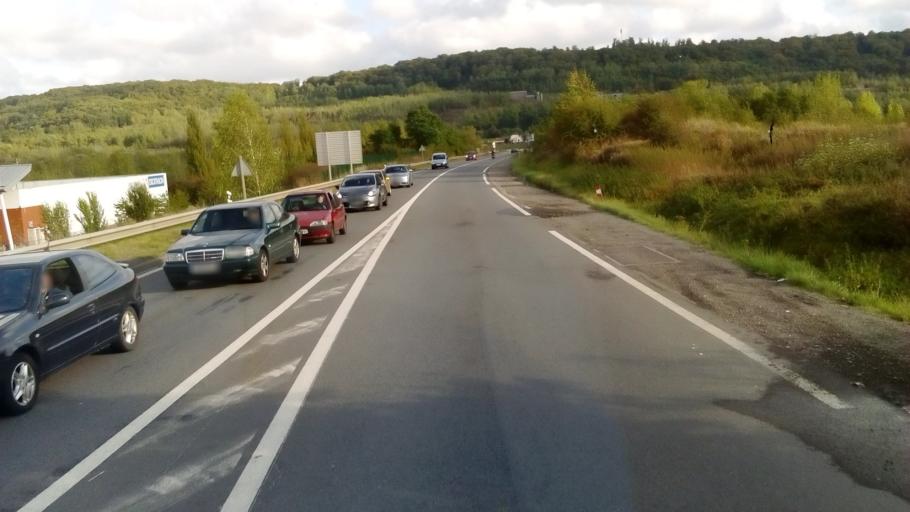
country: FR
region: Lorraine
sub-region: Departement de Meurthe-et-Moselle
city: Mont-Saint-Martin
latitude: 49.5450
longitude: 5.8039
